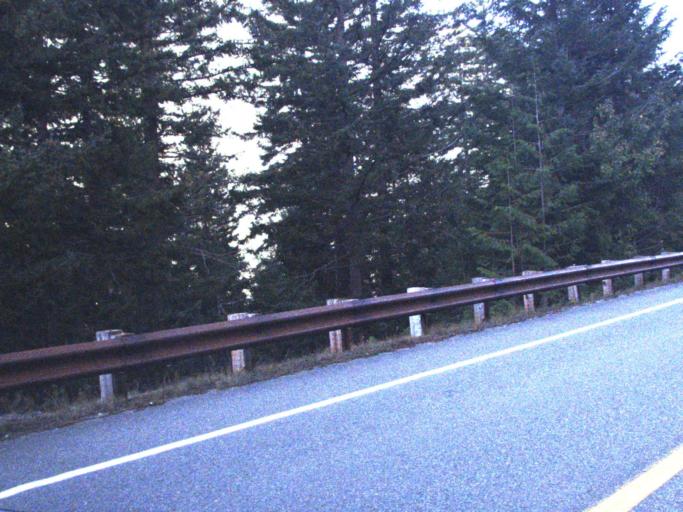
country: US
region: Washington
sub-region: Snohomish County
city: Darrington
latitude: 48.7269
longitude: -121.0364
